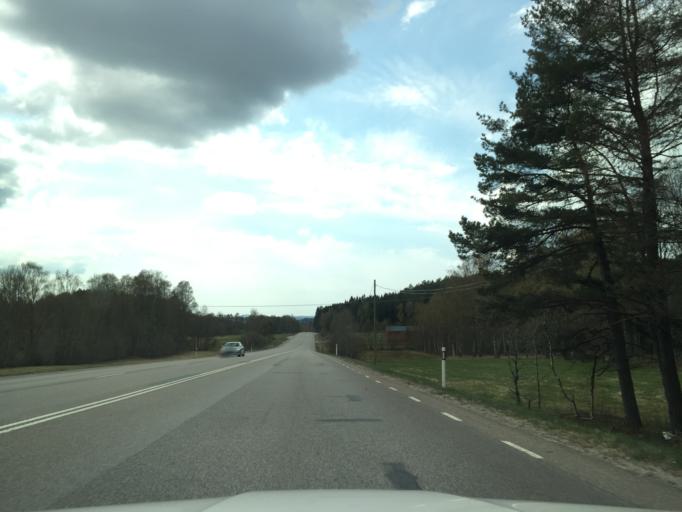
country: SE
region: Vaestra Goetaland
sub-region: Stenungsunds Kommun
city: Stora Hoga
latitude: 58.0545
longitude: 11.9080
